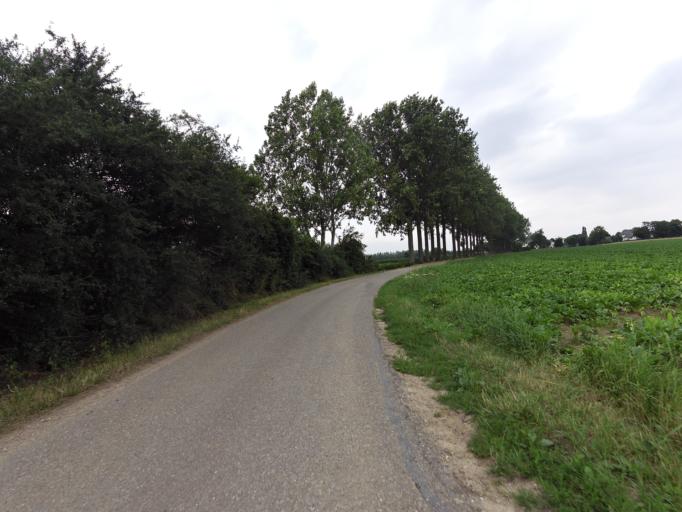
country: NL
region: Gelderland
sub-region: Gemeente Groesbeek
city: Berg en Dal
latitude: 51.8419
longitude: 5.9426
